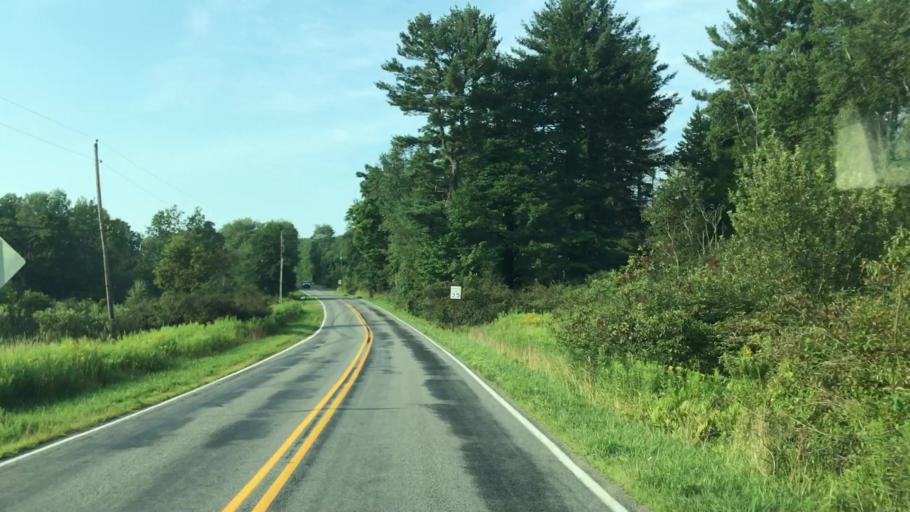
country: US
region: Pennsylvania
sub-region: Lackawanna County
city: Dalton
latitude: 41.6062
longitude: -75.7144
